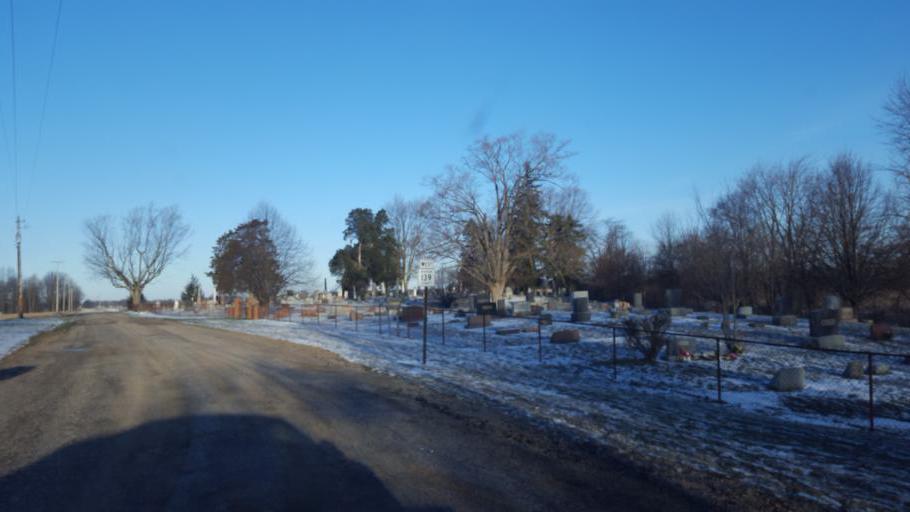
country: US
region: Ohio
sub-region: Morrow County
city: Cardington
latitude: 40.5356
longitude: -82.9194
